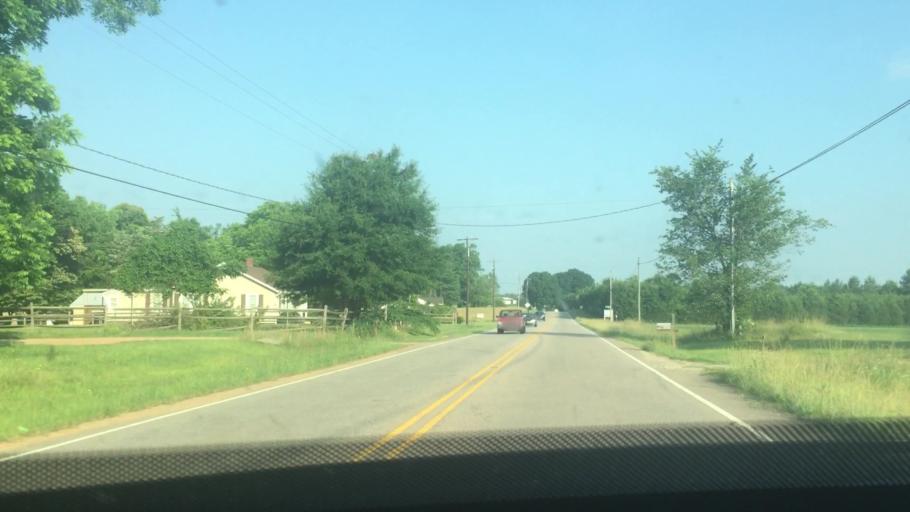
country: US
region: North Carolina
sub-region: Rowan County
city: Enochville
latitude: 35.5805
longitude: -80.7179
